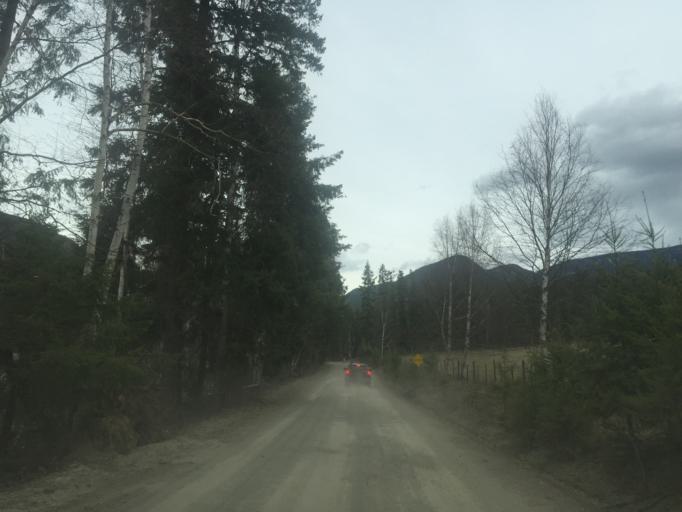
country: CA
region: British Columbia
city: Chase
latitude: 51.3837
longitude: -120.1259
